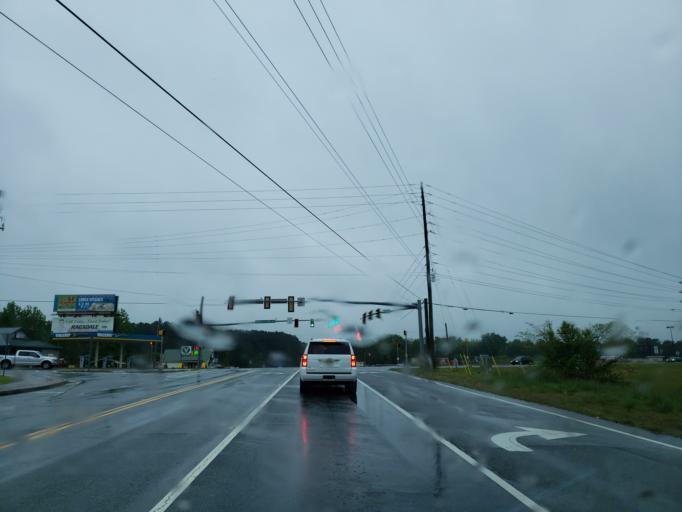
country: US
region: Georgia
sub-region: Carroll County
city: Villa Rica
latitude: 33.8082
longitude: -84.8901
